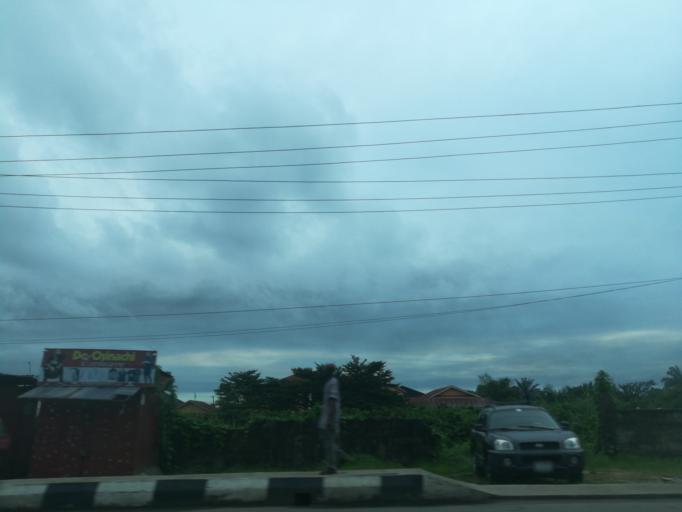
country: NG
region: Rivers
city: Port Harcourt
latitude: 4.8142
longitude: 6.9865
